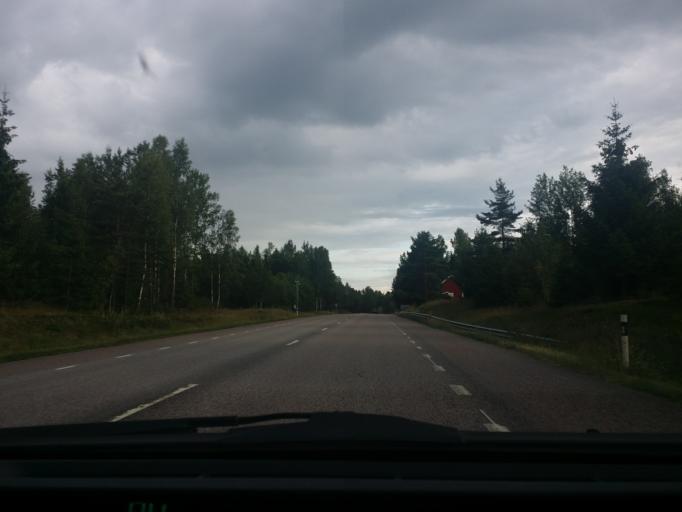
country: SE
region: OErebro
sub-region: Nora Kommun
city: Nora
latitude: 59.4571
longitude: 15.1323
